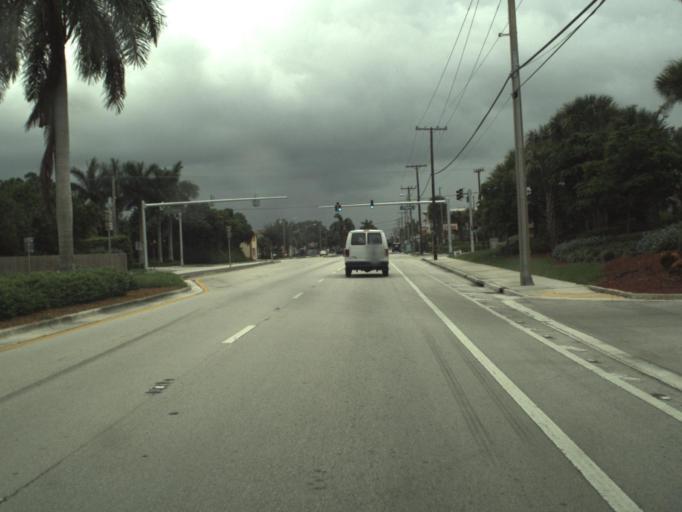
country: US
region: Florida
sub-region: Palm Beach County
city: Delray Beach
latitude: 26.4924
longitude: -80.0630
